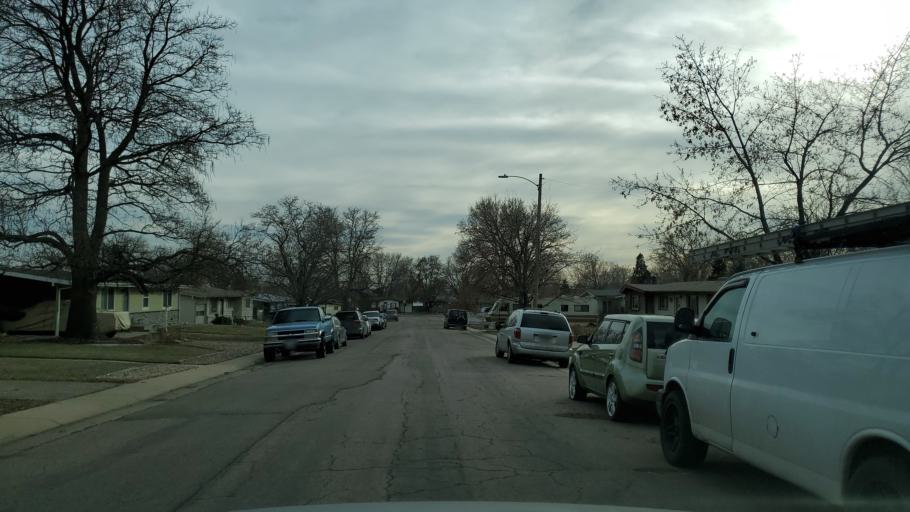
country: US
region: Colorado
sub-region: Adams County
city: Sherrelwood
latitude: 39.8385
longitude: -105.0174
